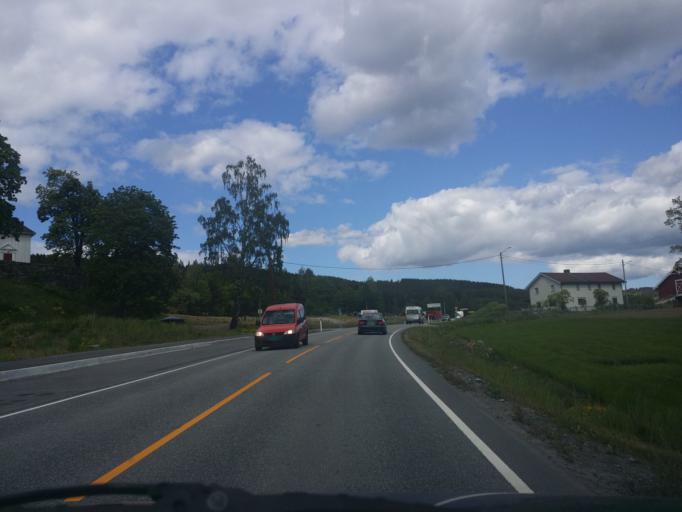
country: NO
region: Oppland
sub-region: Jevnaker
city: Jevnaker
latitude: 60.2568
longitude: 10.4344
